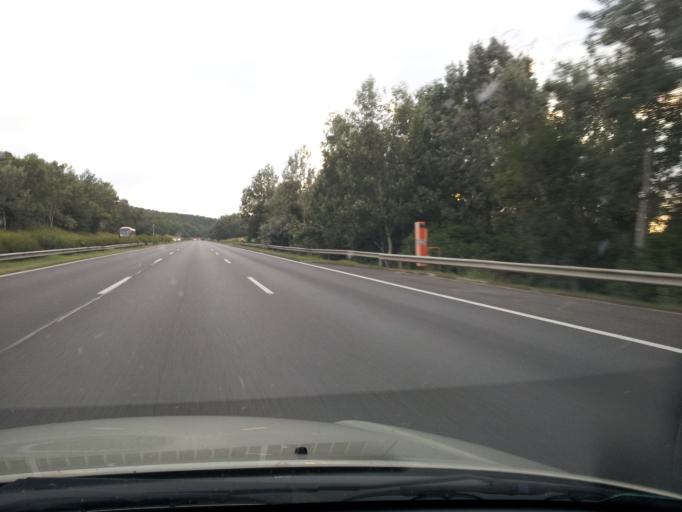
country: HU
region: Pest
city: Godollo
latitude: 47.6126
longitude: 19.3915
